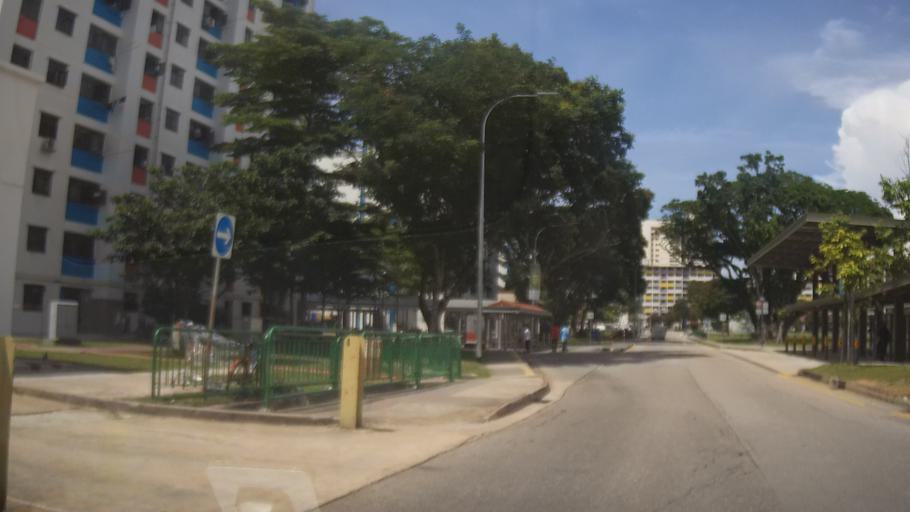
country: SG
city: Singapore
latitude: 1.3276
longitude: 103.8827
